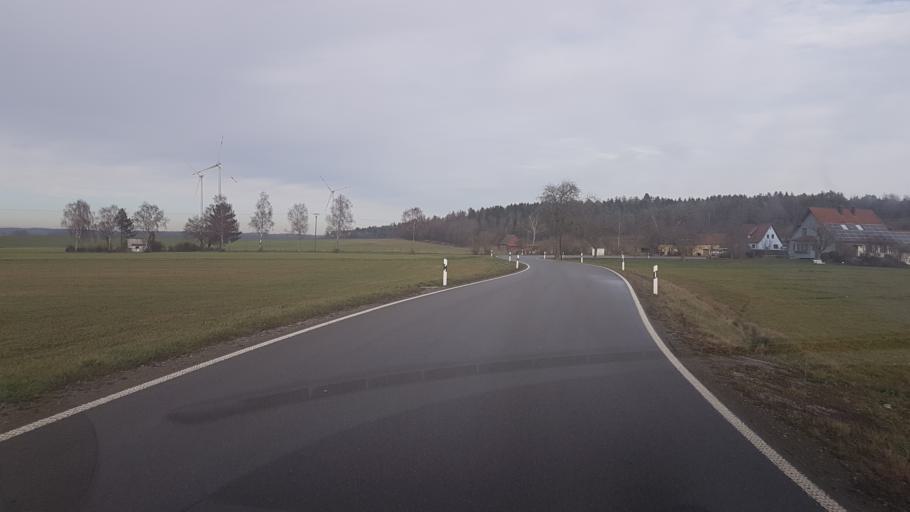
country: DE
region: Baden-Wuerttemberg
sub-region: Regierungsbezirk Stuttgart
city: Wallhausen
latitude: 49.2316
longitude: 10.0582
